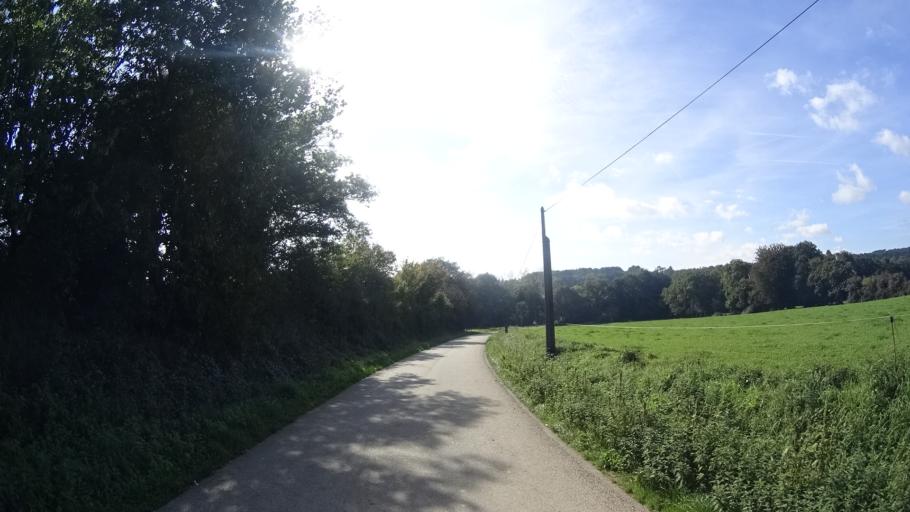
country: FR
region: Brittany
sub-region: Departement du Morbihan
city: La Gacilly
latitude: 47.7651
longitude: -2.1876
